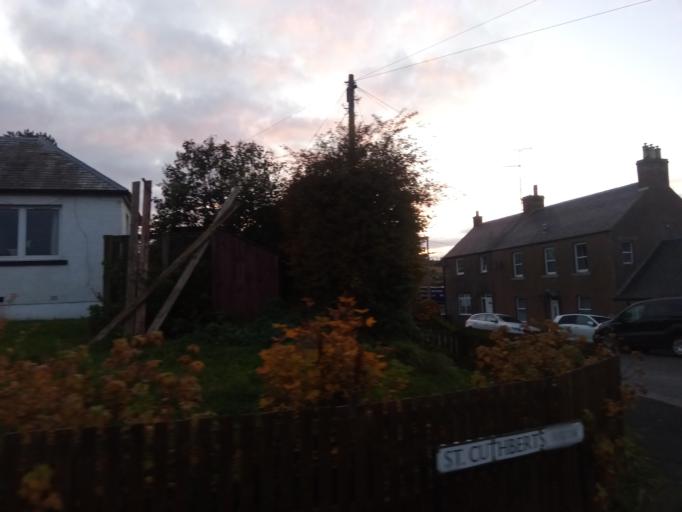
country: GB
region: Scotland
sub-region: The Scottish Borders
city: Lauder
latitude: 55.7719
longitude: -2.8048
